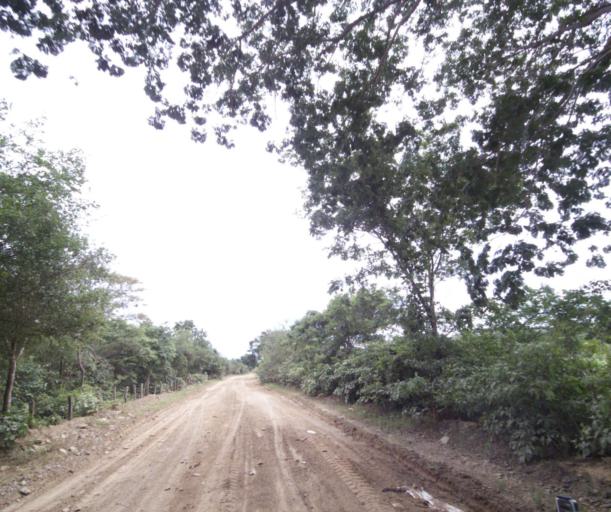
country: BR
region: Bahia
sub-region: Carinhanha
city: Carinhanha
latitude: -14.2248
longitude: -44.2996
